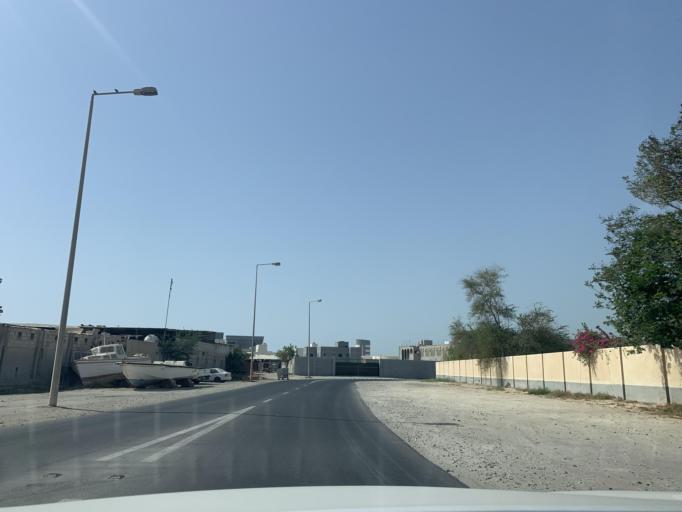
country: BH
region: Manama
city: Jidd Hafs
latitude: 26.2272
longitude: 50.4631
